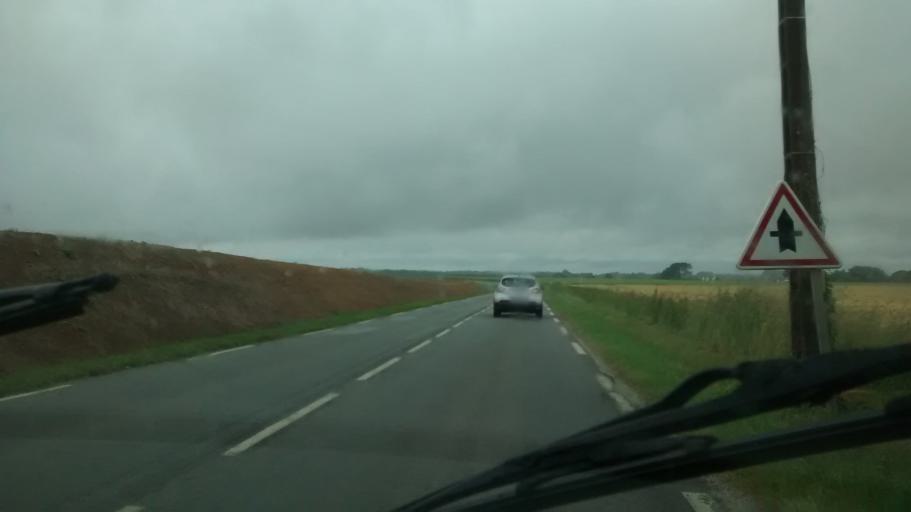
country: FR
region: Brittany
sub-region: Departement du Morbihan
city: Ploemeur
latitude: 47.7557
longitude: -3.4207
